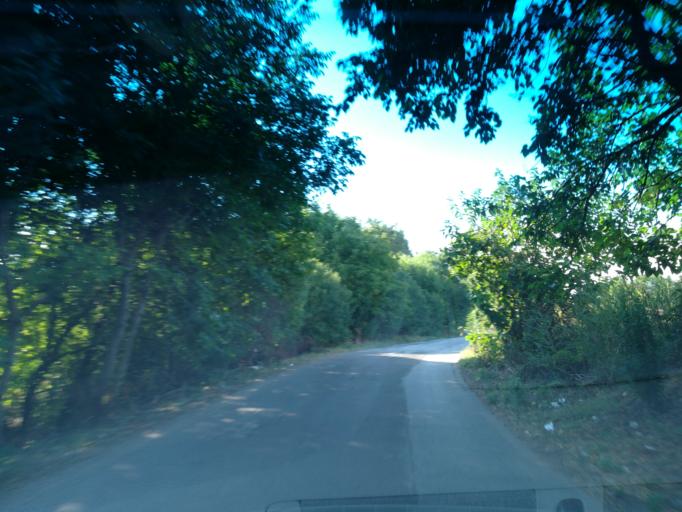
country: BG
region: Stara Zagora
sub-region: Obshtina Chirpan
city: Chirpan
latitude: 42.0571
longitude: 25.2677
